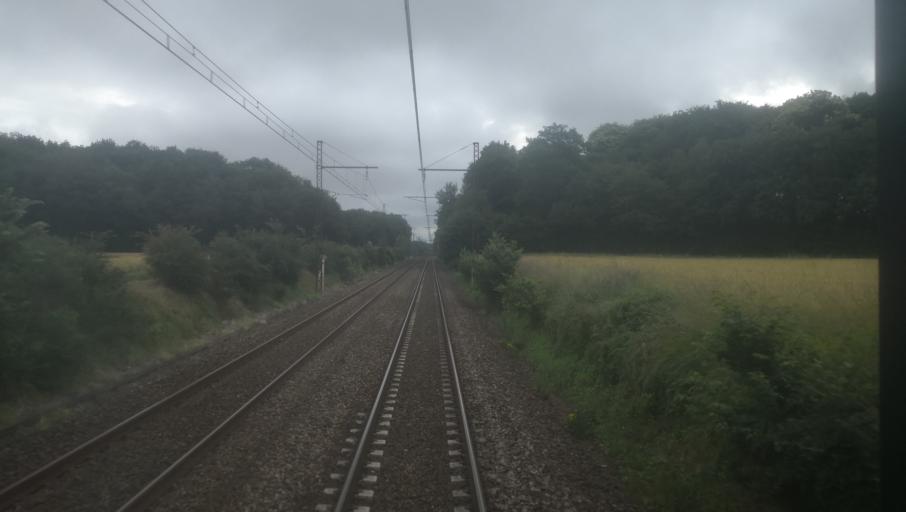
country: FR
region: Centre
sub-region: Departement de l'Indre
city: Montierchaume
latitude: 46.8334
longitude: 1.7553
